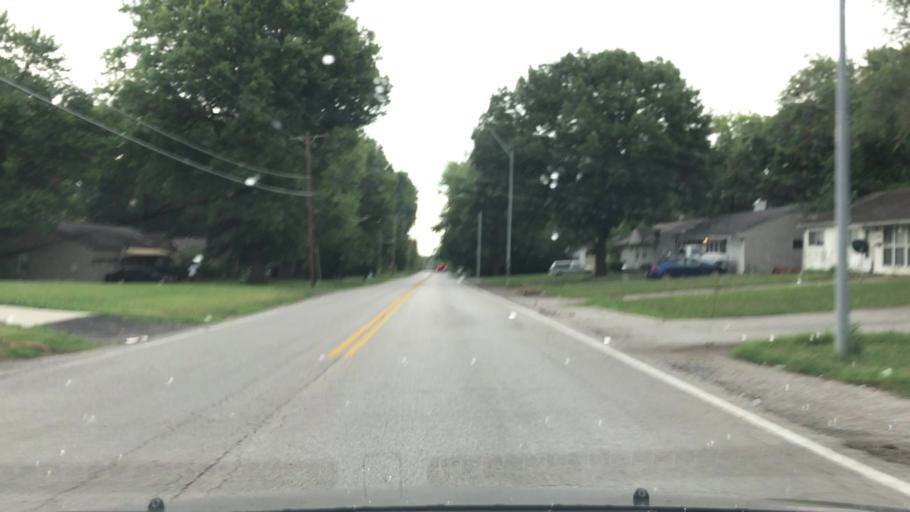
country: US
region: Missouri
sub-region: Jackson County
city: Grandview
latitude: 38.9303
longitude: -94.5019
